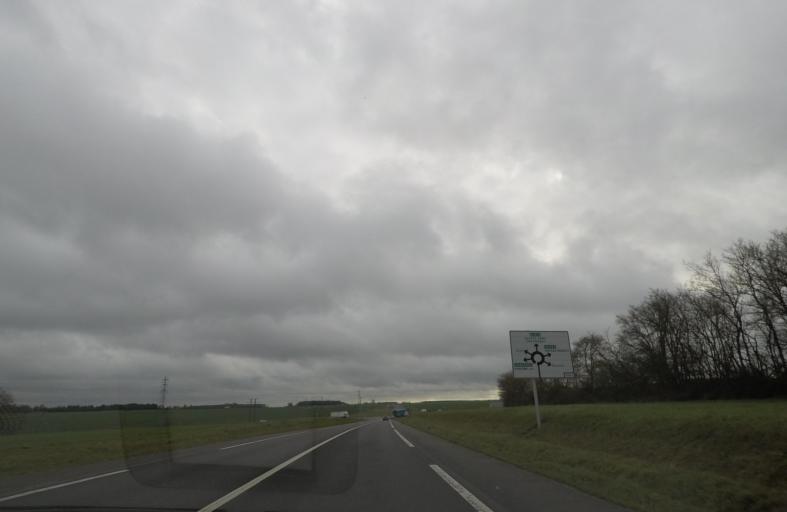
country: FR
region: Centre
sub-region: Departement du Loir-et-Cher
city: Vendome
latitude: 47.7733
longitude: 1.0570
